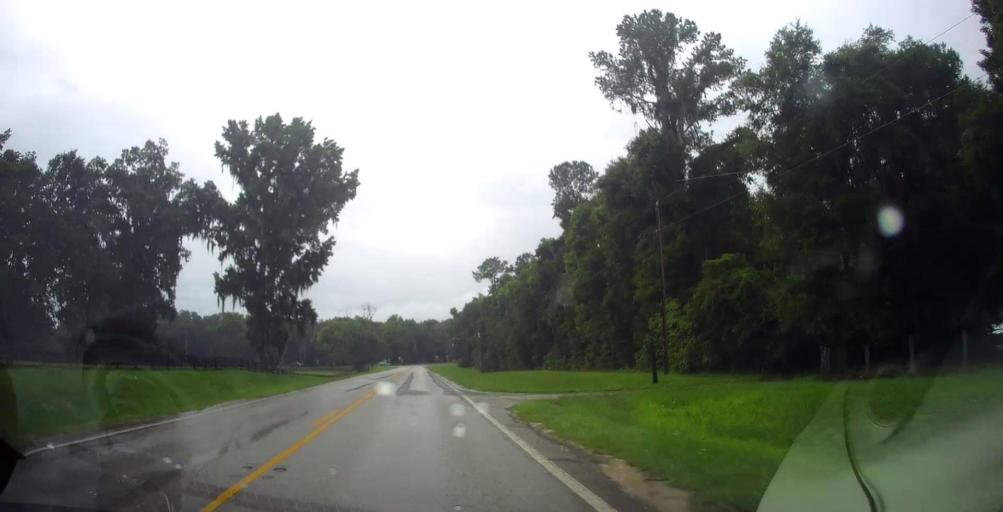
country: US
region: Florida
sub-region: Marion County
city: Citra
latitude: 29.3628
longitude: -82.2514
